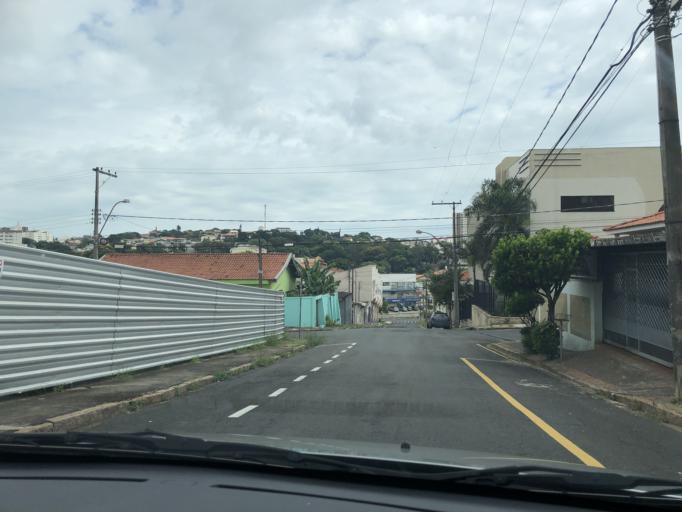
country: BR
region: Sao Paulo
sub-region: Americana
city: Americana
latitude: -22.7361
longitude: -47.3342
